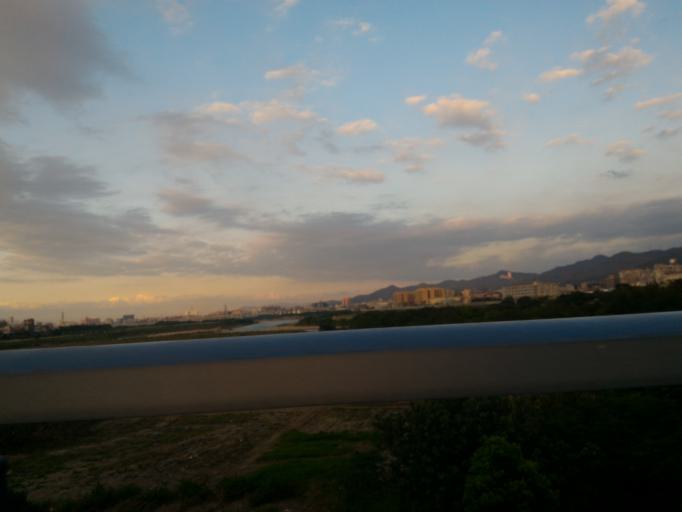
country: TW
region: Taipei
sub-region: Taipei
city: Banqiao
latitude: 24.9643
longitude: 121.4049
